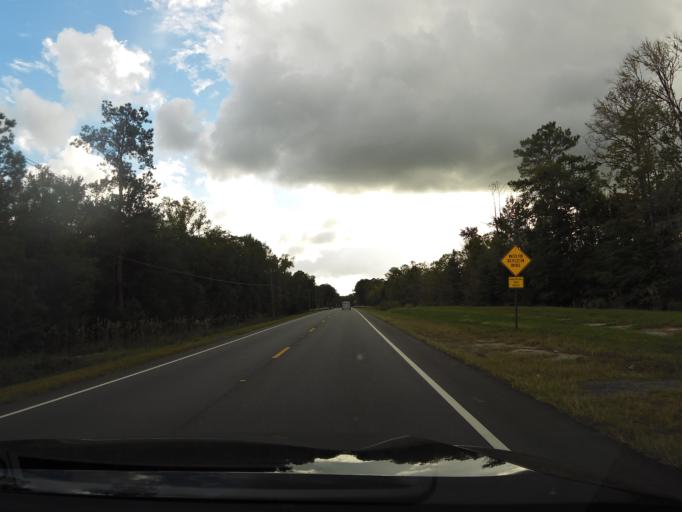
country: US
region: Georgia
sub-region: Liberty County
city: Midway
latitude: 31.8352
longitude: -81.4191
